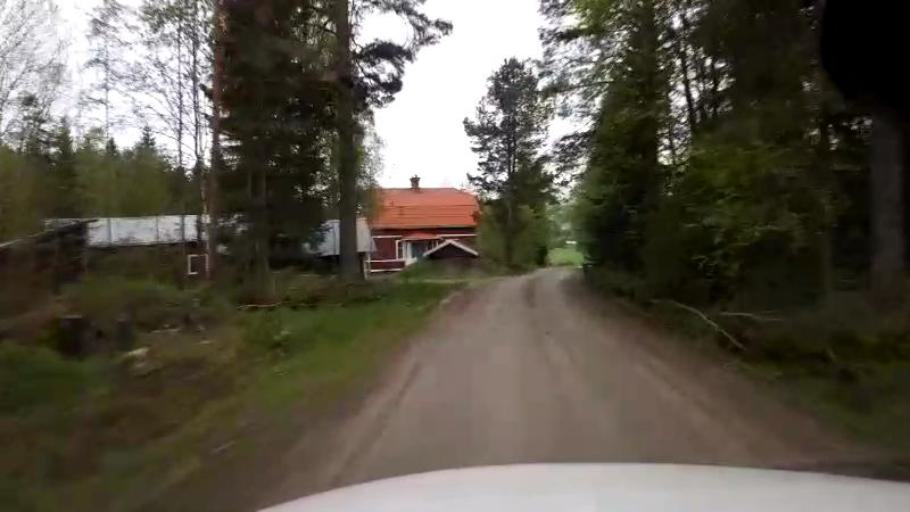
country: SE
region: Gaevleborg
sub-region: Ljusdals Kommun
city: Jaervsoe
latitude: 61.7651
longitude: 16.1836
